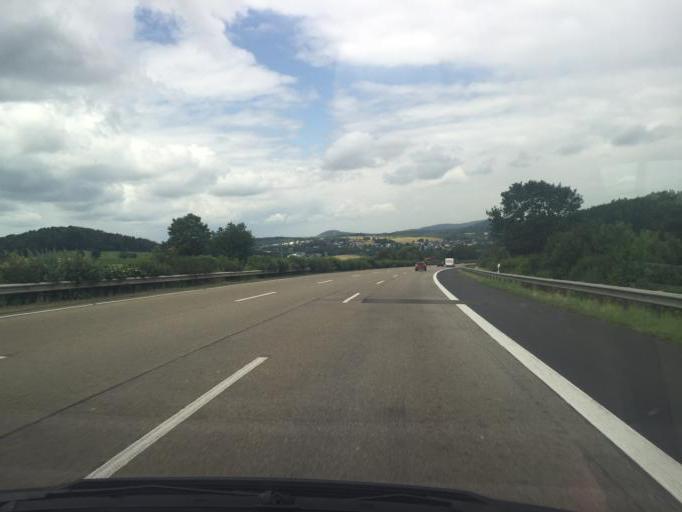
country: DE
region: Rheinland-Pfalz
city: Nomborn
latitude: 50.4313
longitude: 7.9215
